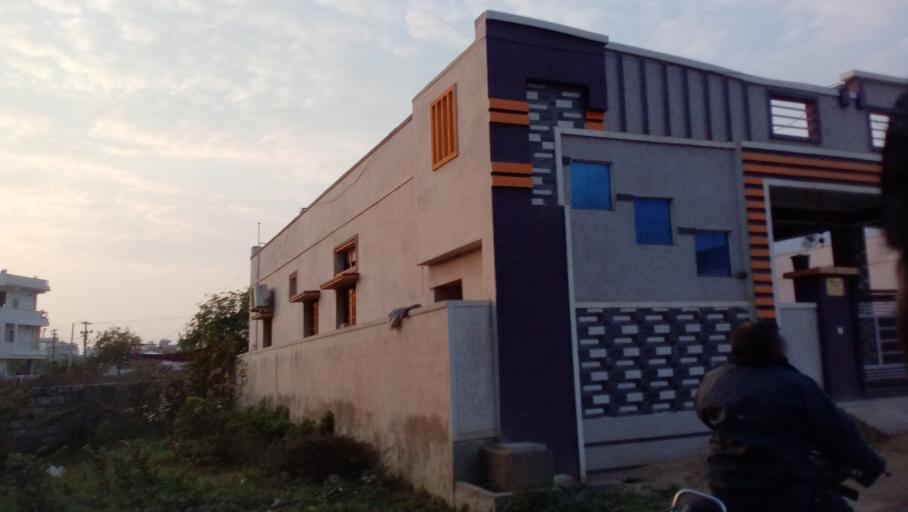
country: IN
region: Telangana
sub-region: Medak
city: Serilingampalle
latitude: 17.5182
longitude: 78.3140
